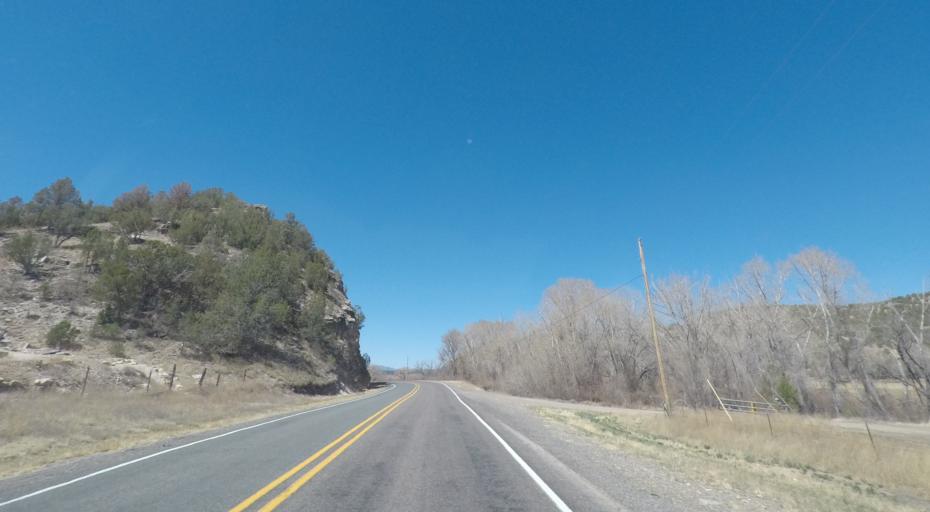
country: US
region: New Mexico
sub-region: Lincoln County
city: Capitan
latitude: 33.5232
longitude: -105.4652
